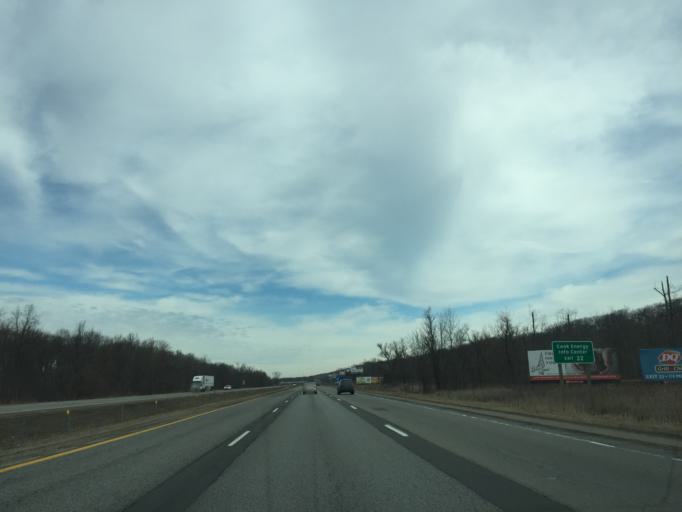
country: US
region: Michigan
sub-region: Berrien County
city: Stevensville
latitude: 41.9976
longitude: -86.5370
